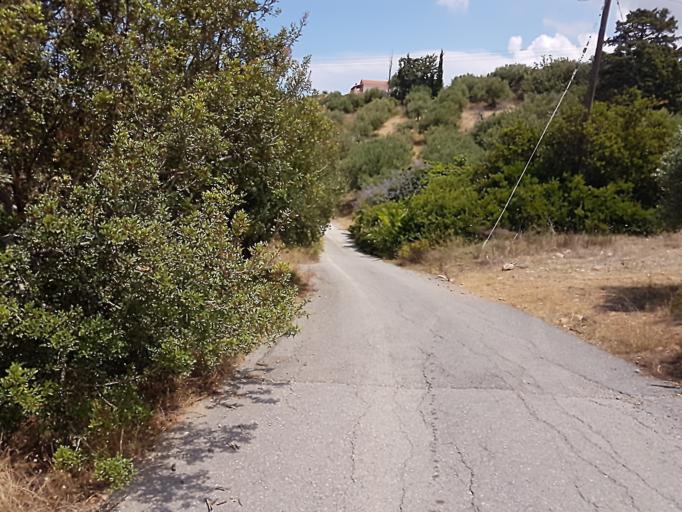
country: GR
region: Crete
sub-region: Nomos Irakleiou
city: Limin Khersonisou
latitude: 35.3099
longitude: 25.3800
